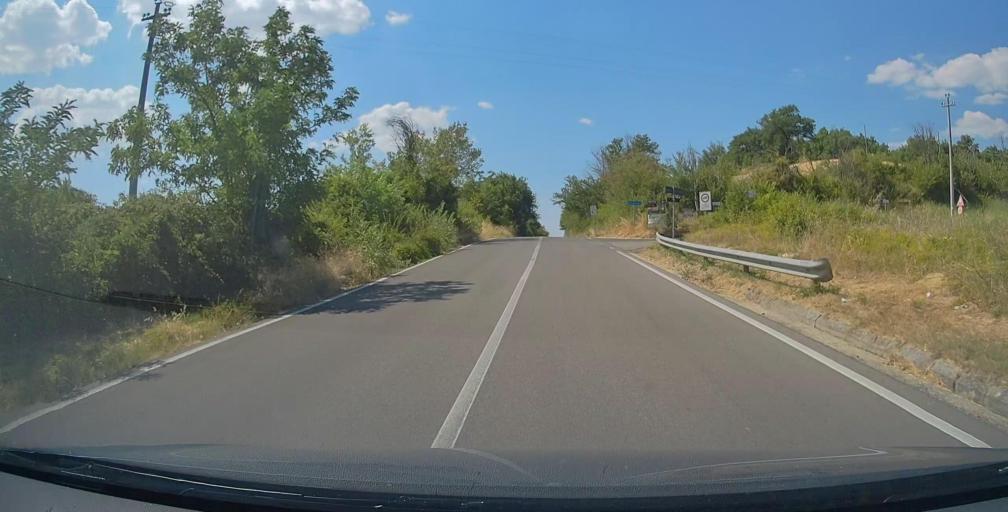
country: IT
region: Umbria
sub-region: Provincia di Terni
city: Otricoli
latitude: 42.3928
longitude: 12.4677
